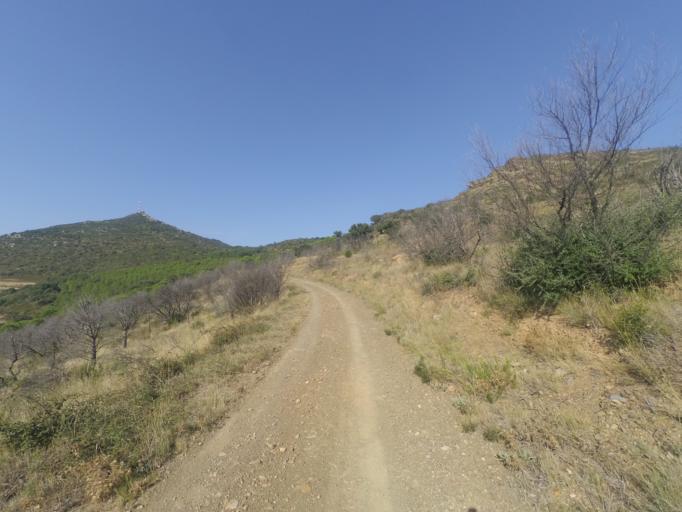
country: FR
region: Languedoc-Roussillon
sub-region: Departement des Pyrenees-Orientales
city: Corneilla-la-Riviere
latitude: 42.7307
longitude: 2.7126
